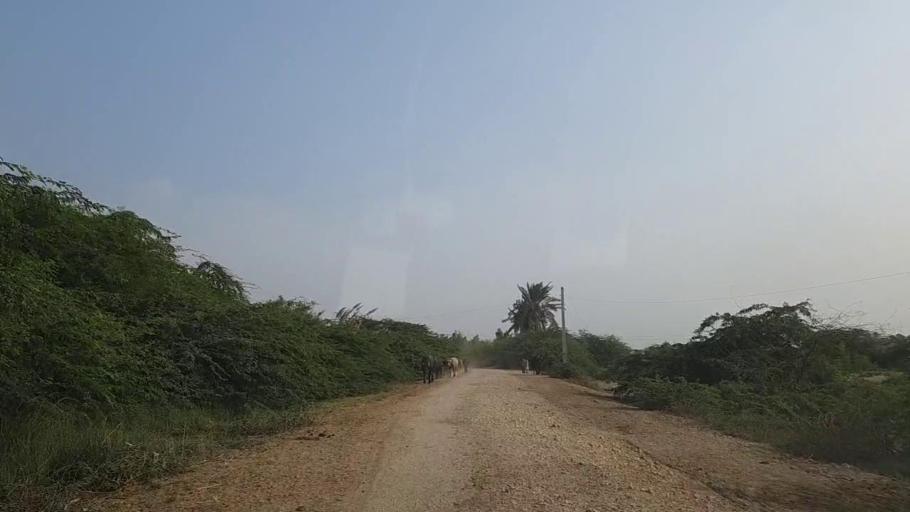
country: PK
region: Sindh
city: Gharo
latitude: 24.6527
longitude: 67.6202
